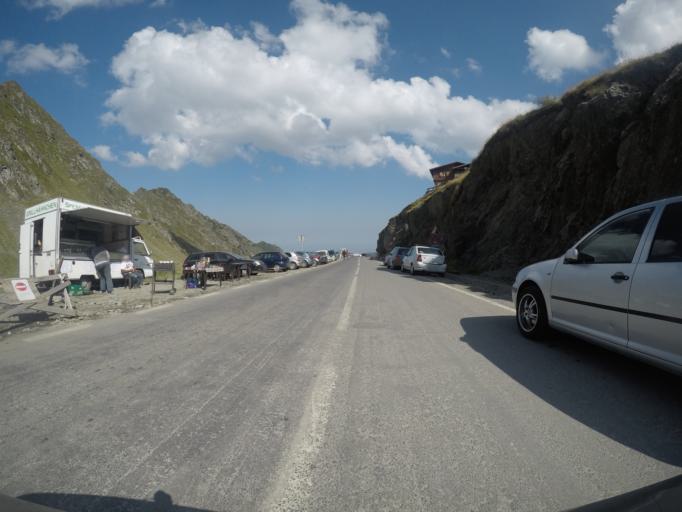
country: RO
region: Sibiu
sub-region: Comuna Cartisoara
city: Cartisoara
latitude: 45.6039
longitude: 24.6137
